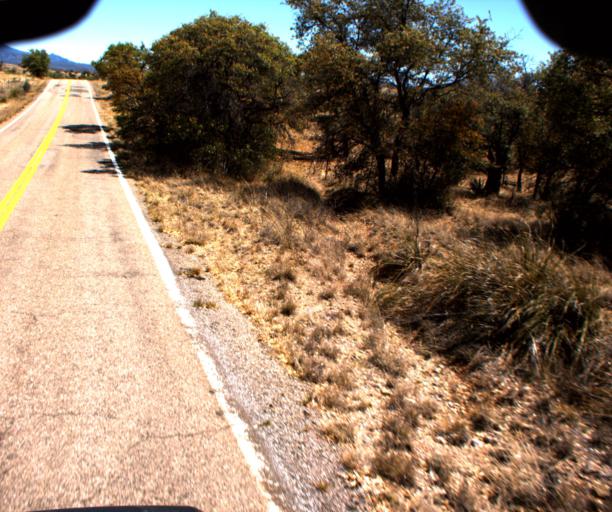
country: US
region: Arizona
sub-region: Cochise County
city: Huachuca City
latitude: 31.5823
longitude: -110.5593
